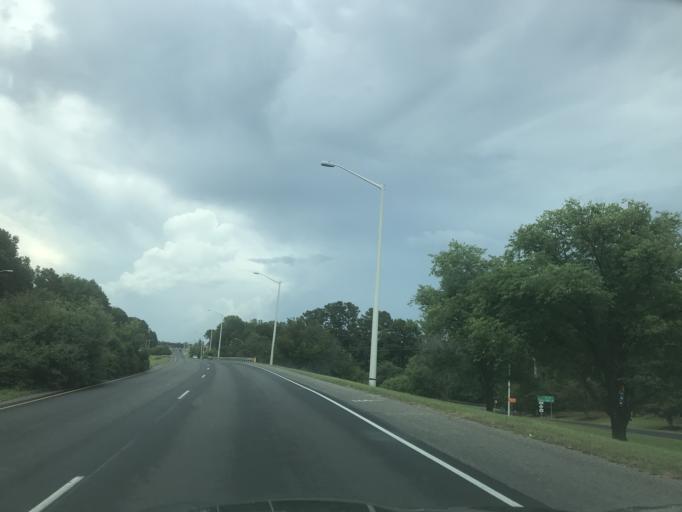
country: US
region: North Carolina
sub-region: Johnston County
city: Clayton
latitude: 35.6461
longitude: -78.4644
